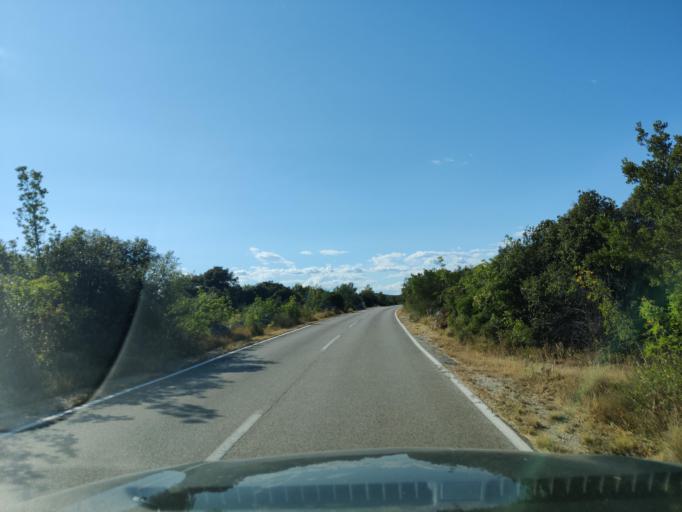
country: HR
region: Sibensko-Kniniska
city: Zaton
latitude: 43.7473
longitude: 15.8444
